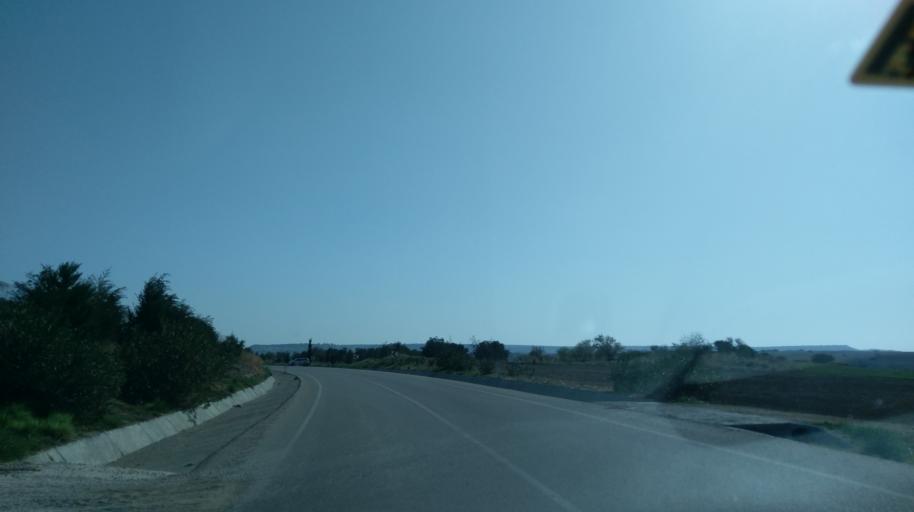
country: CY
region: Ammochostos
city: Leonarisso
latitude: 35.3877
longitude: 34.0108
